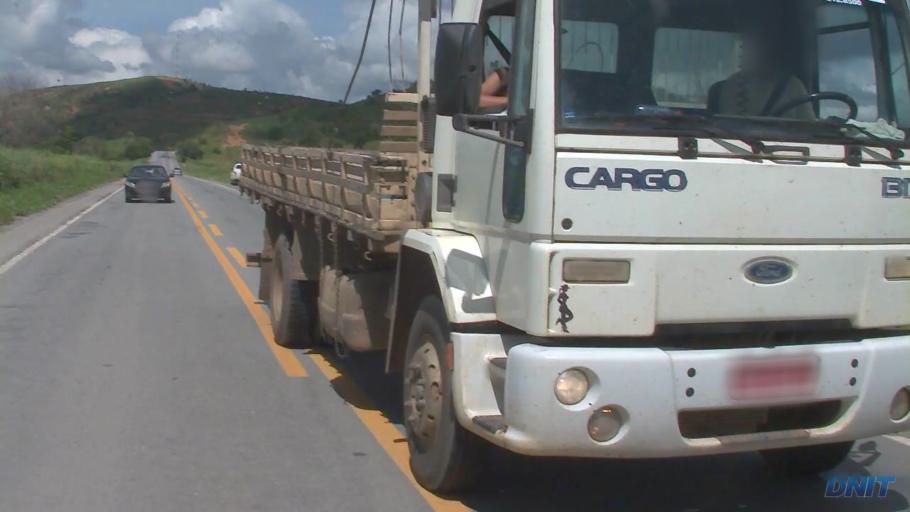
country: BR
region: Minas Gerais
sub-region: Governador Valadares
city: Governador Valadares
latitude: -19.0173
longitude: -42.1416
